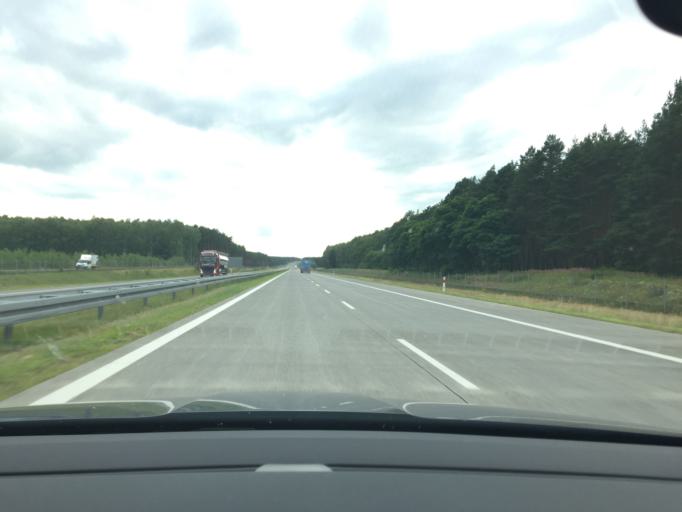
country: PL
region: Lubusz
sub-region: Powiat swiebodzinski
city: Swiebodzin
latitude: 52.3225
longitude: 15.5198
